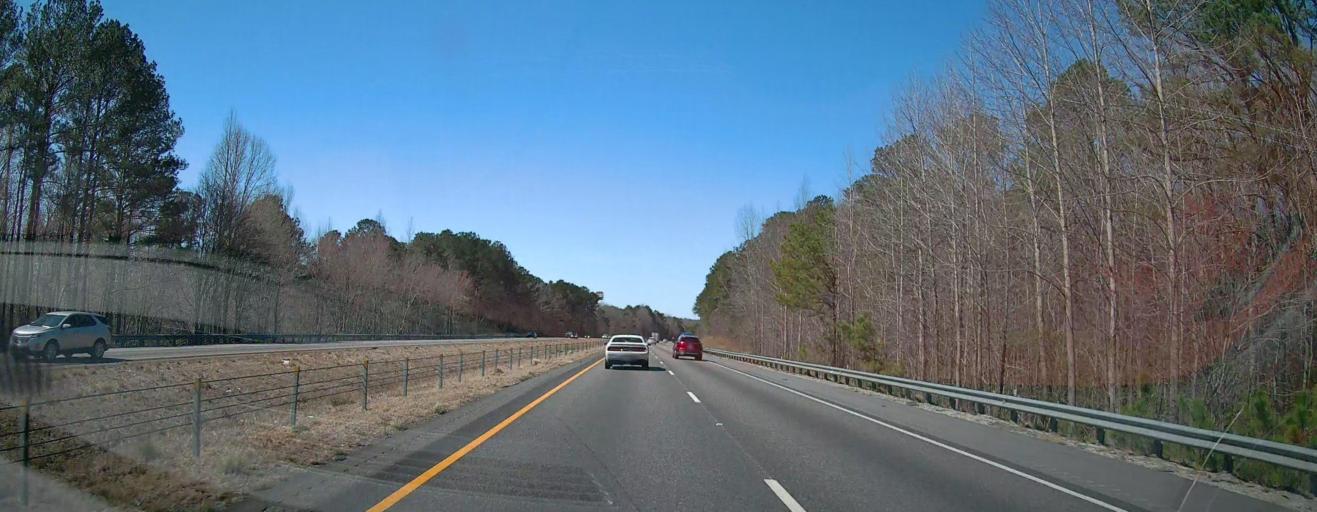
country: US
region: Alabama
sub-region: Cleburne County
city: Heflin
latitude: 33.6223
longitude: -85.5781
